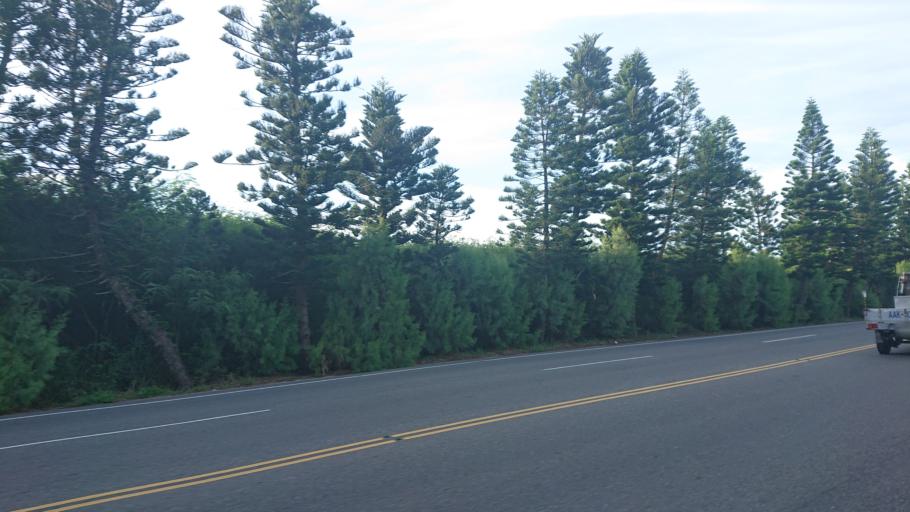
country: TW
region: Taiwan
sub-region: Penghu
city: Ma-kung
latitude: 23.6598
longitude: 119.5568
